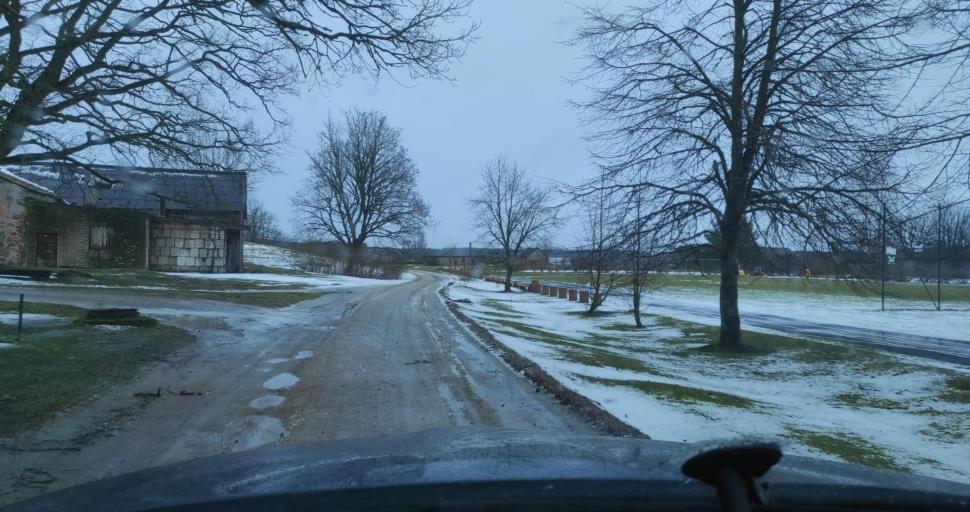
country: LV
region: Dundaga
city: Dundaga
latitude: 57.5141
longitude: 22.0244
